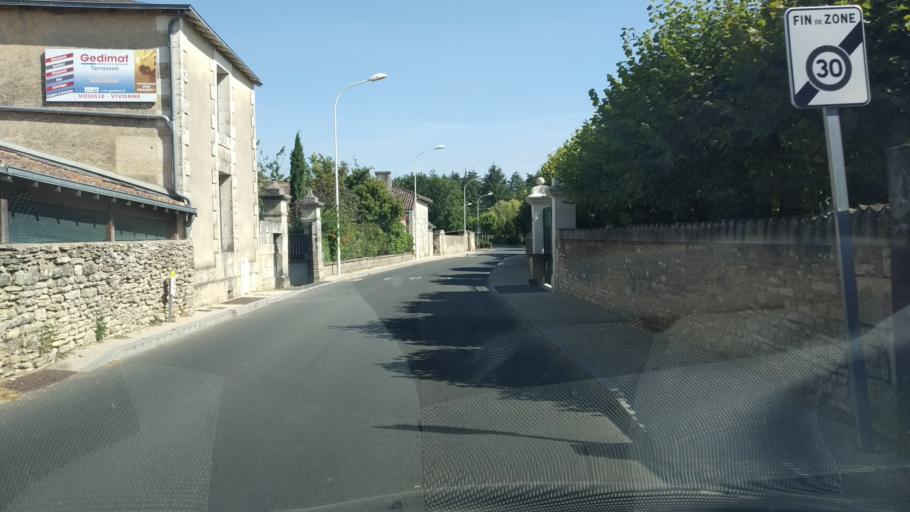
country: FR
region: Poitou-Charentes
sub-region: Departement de la Vienne
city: Cisse
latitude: 46.6448
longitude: 0.2311
